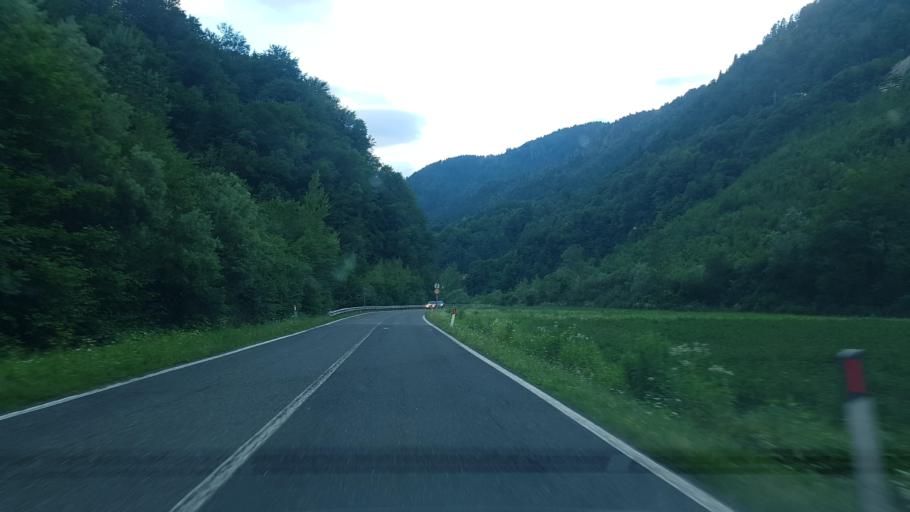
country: IT
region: Friuli Venezia Giulia
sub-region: Provincia di Udine
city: Zuglio
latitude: 46.4741
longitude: 13.0809
